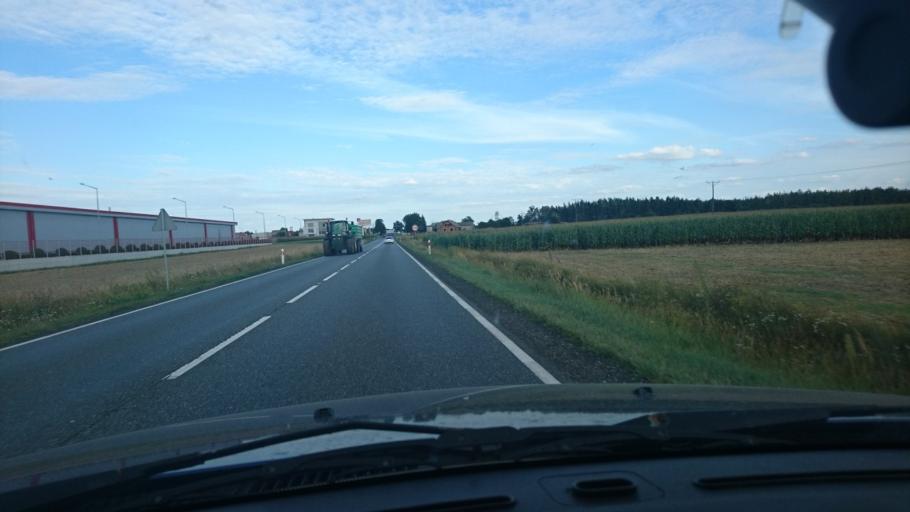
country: PL
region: Greater Poland Voivodeship
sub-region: Powiat kepinski
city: Slupia pod Kepnem
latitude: 51.2318
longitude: 18.0688
